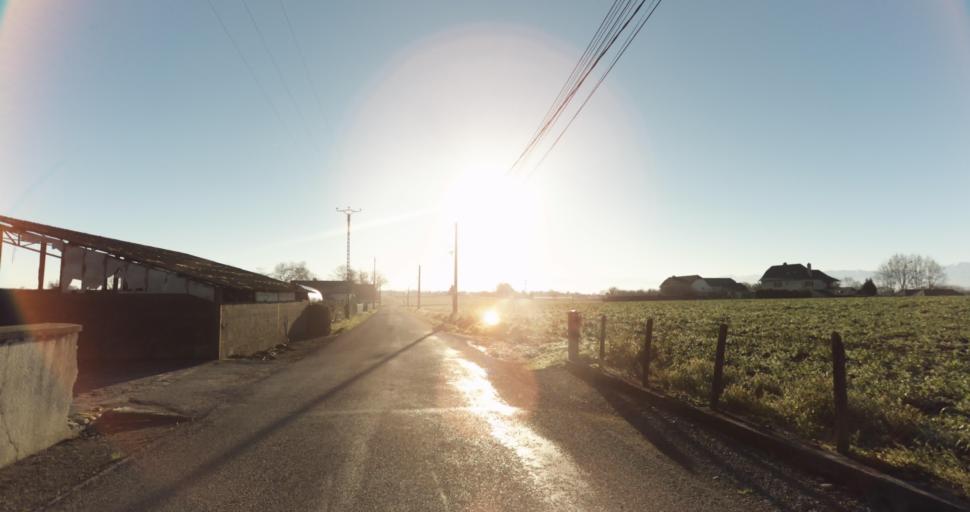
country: FR
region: Aquitaine
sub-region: Departement des Pyrenees-Atlantiques
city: Morlaas
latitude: 43.3222
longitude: -0.2518
